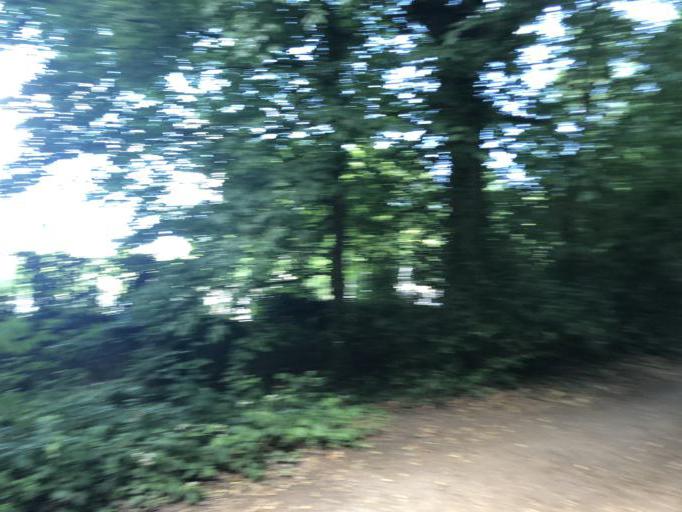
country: GB
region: England
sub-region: Greater London
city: Wandsworth
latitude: 51.4391
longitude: -0.2382
